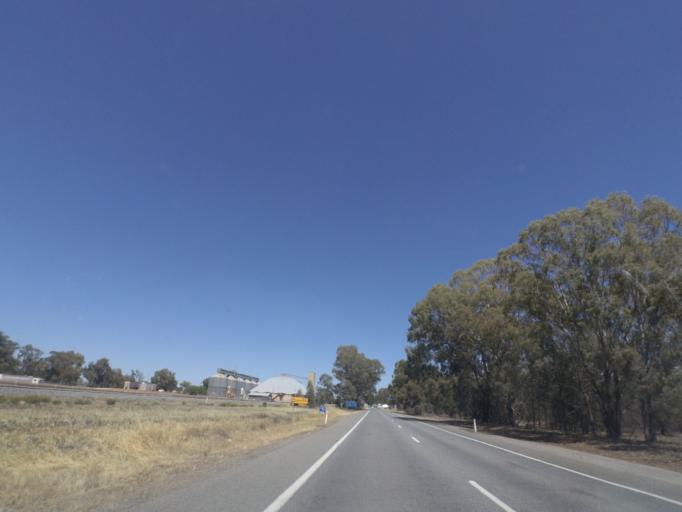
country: AU
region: New South Wales
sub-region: Narrandera
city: Narrandera
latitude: -34.7388
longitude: 146.5736
